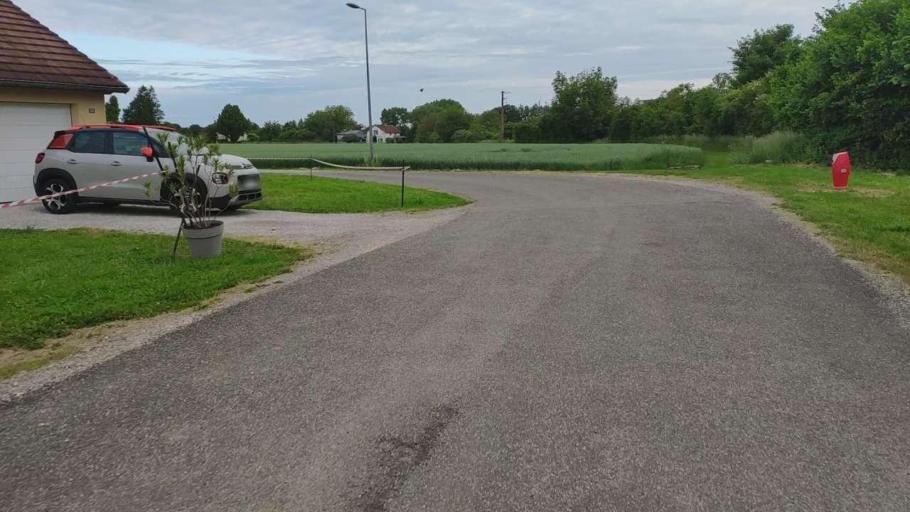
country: FR
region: Franche-Comte
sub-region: Departement du Jura
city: Bletterans
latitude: 46.7490
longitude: 5.4610
